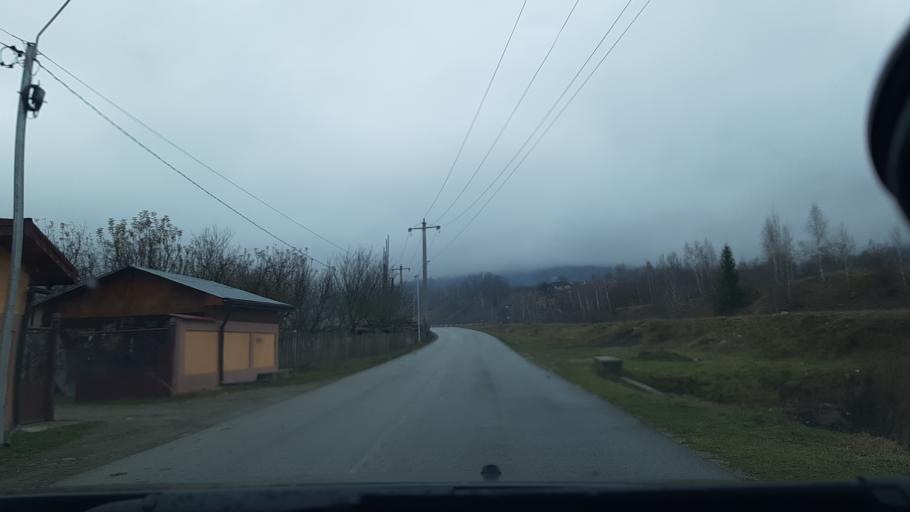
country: RO
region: Hunedoara
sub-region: Oras Petrila
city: Petrila
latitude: 45.4240
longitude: 23.4249
